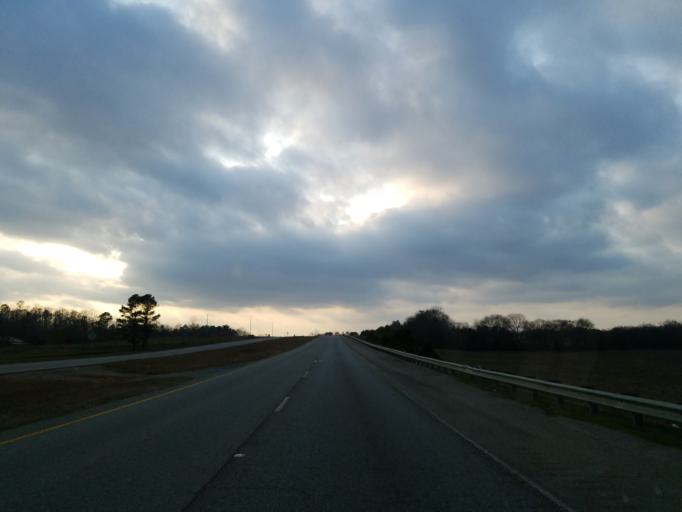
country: US
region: Georgia
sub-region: Bartow County
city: Euharlee
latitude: 34.0969
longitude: -84.9443
